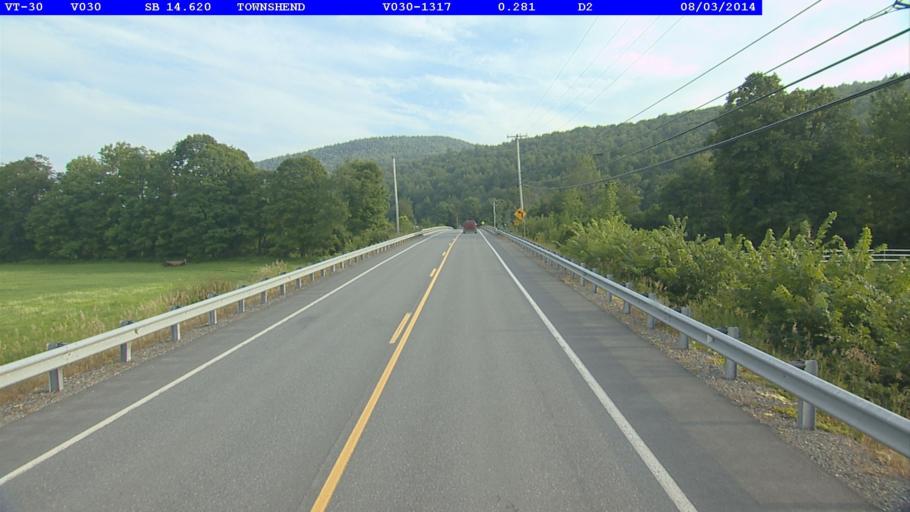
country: US
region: Vermont
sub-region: Windham County
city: Newfane
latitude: 43.0233
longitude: -72.6570
